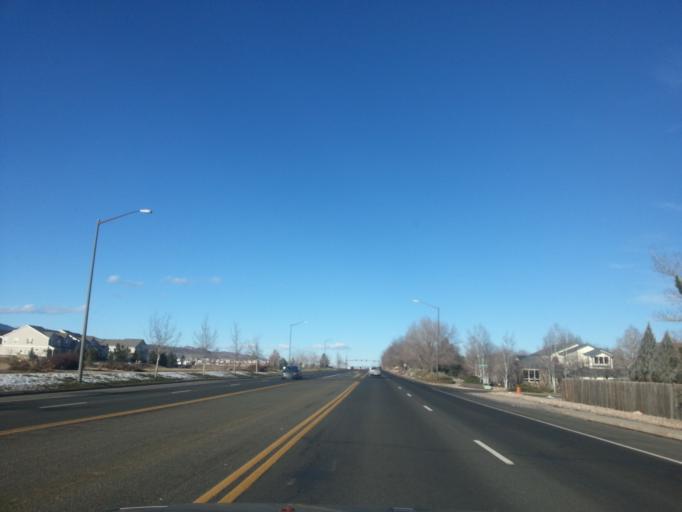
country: US
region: Colorado
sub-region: Larimer County
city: Loveland
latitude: 40.4244
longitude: -105.1156
